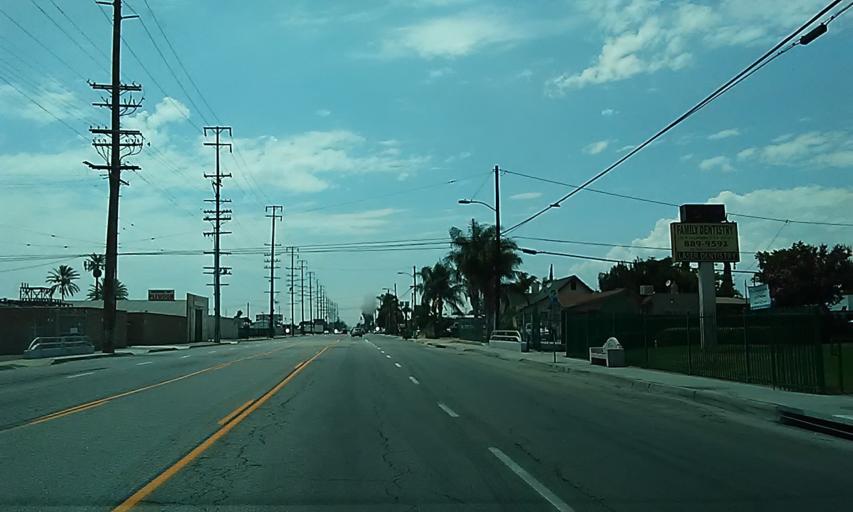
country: US
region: California
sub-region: San Bernardino County
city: San Bernardino
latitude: 34.1214
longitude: -117.2576
